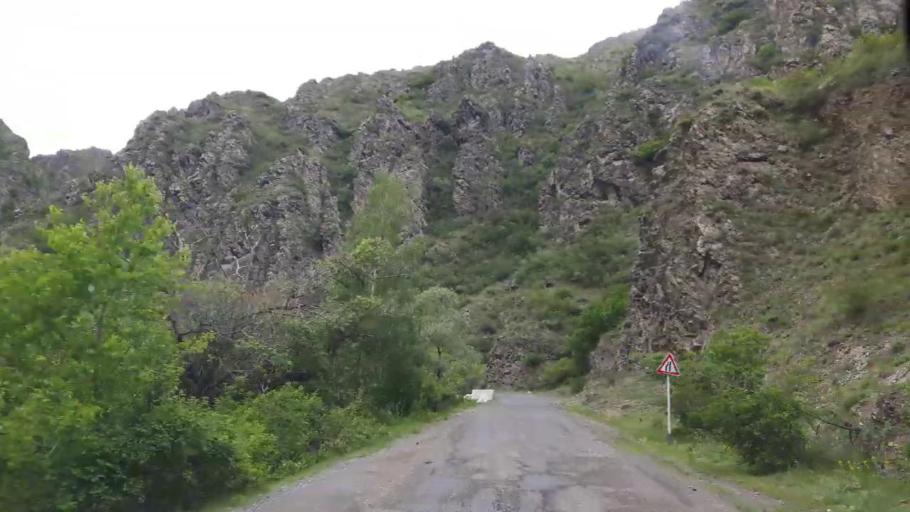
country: GE
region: Shida Kartli
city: Gori
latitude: 41.9002
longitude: 44.0661
